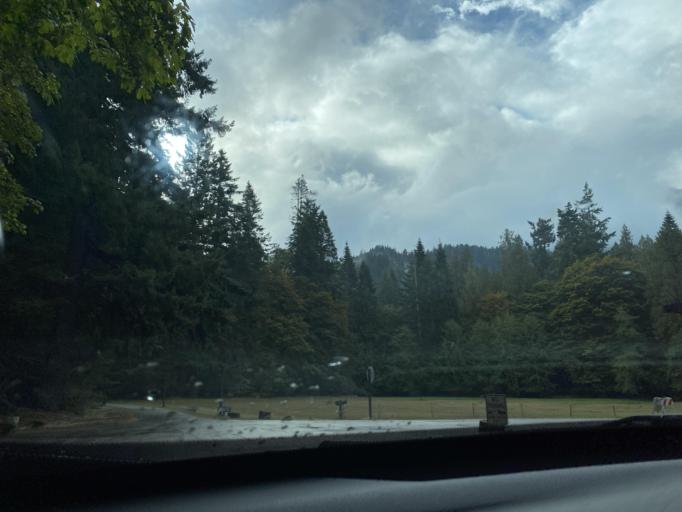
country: CA
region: British Columbia
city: Sooke
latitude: 48.0578
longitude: -123.7990
